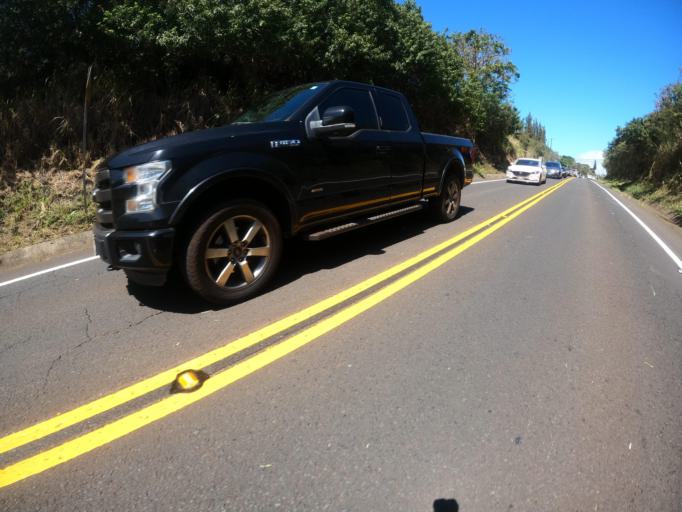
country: US
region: Hawaii
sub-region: Honolulu County
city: Schofield Barracks
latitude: 21.4789
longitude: -158.0497
